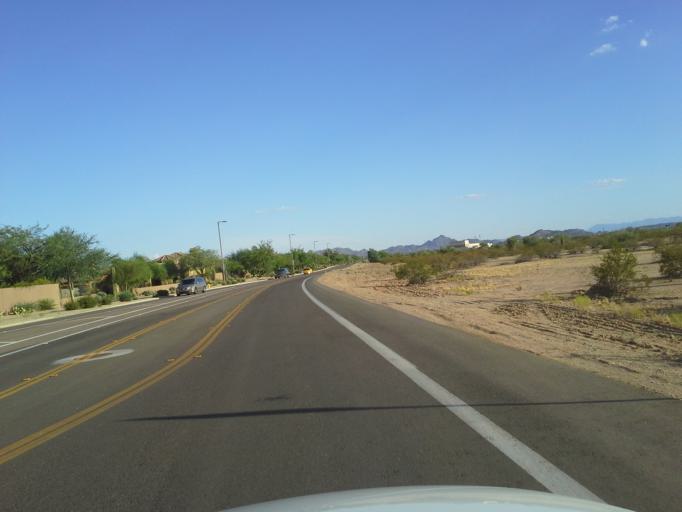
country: US
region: Arizona
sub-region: Maricopa County
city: Cave Creek
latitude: 33.6912
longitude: -112.0053
